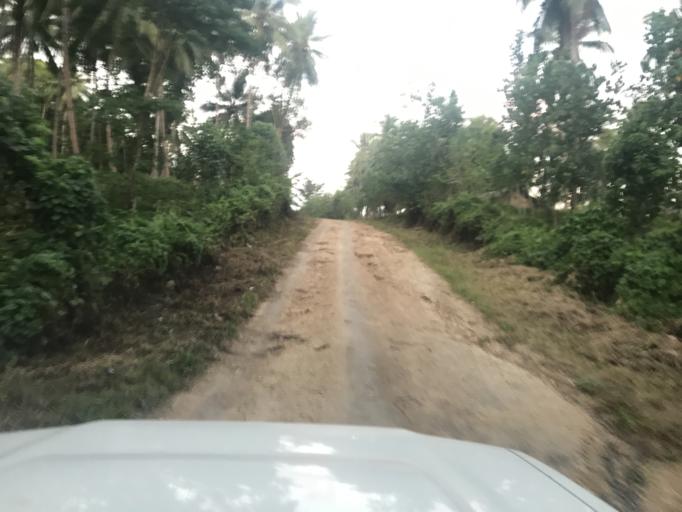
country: VU
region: Sanma
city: Luganville
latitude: -15.5537
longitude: 166.9814
